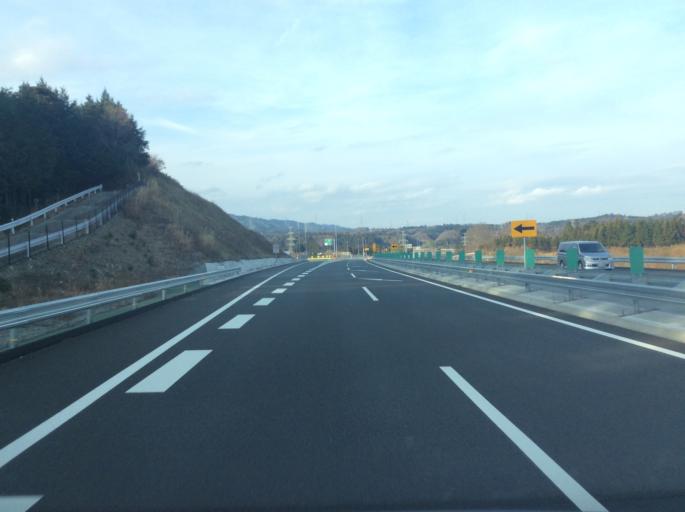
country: JP
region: Fukushima
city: Namie
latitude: 37.4966
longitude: 140.9436
